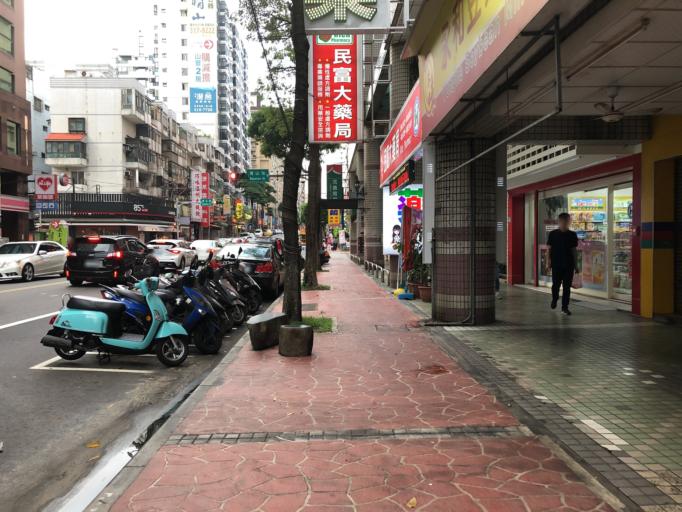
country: TW
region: Taiwan
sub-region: Taoyuan
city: Taoyuan
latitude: 25.0126
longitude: 121.3183
